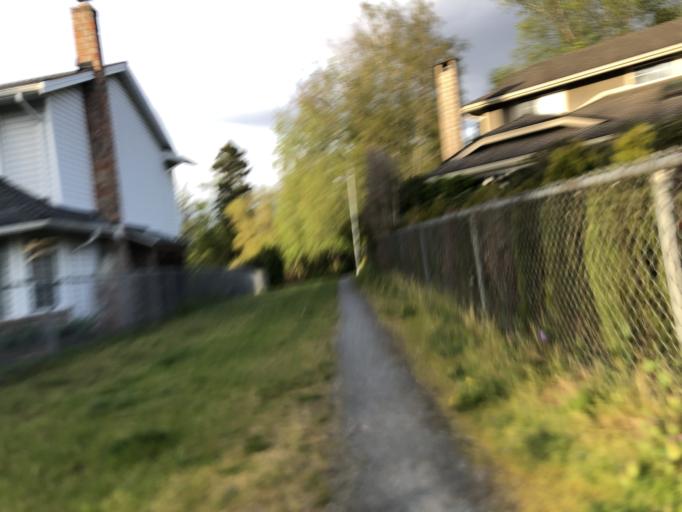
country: CA
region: British Columbia
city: Richmond
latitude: 49.1453
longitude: -123.1079
